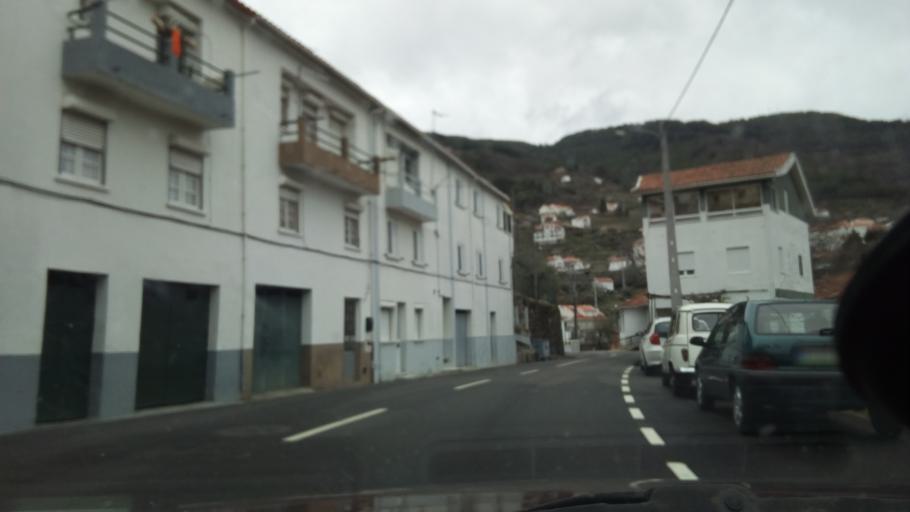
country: PT
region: Guarda
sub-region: Manteigas
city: Manteigas
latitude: 40.3991
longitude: -7.5428
